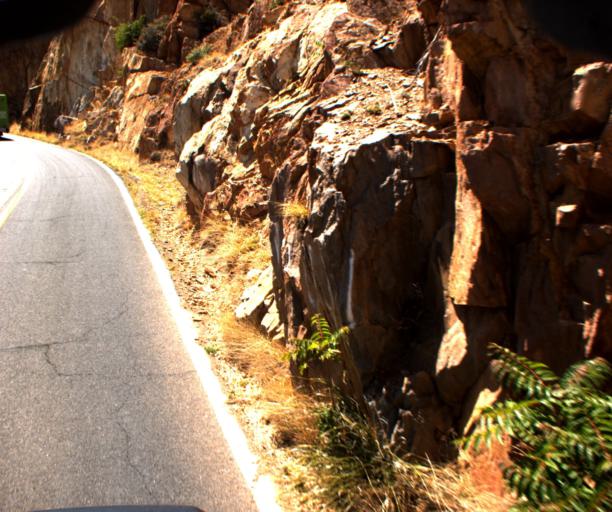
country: US
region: Arizona
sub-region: Yavapai County
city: Clarkdale
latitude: 34.7447
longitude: -112.1175
